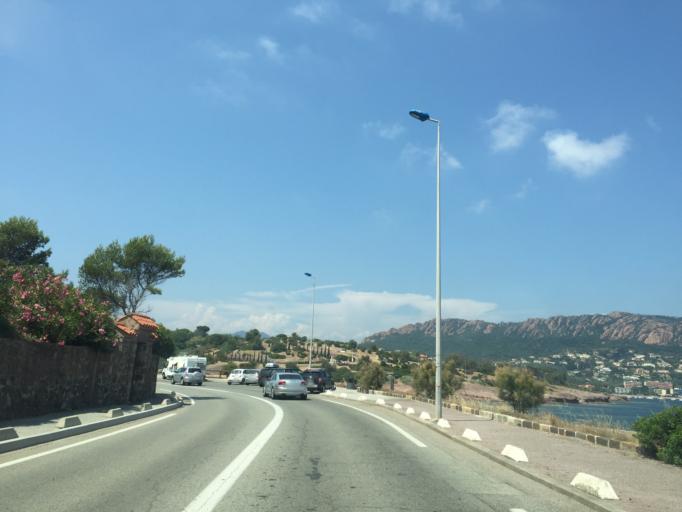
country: FR
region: Provence-Alpes-Cote d'Azur
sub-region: Departement du Var
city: Saint-Raphael
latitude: 43.4235
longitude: 6.8576
